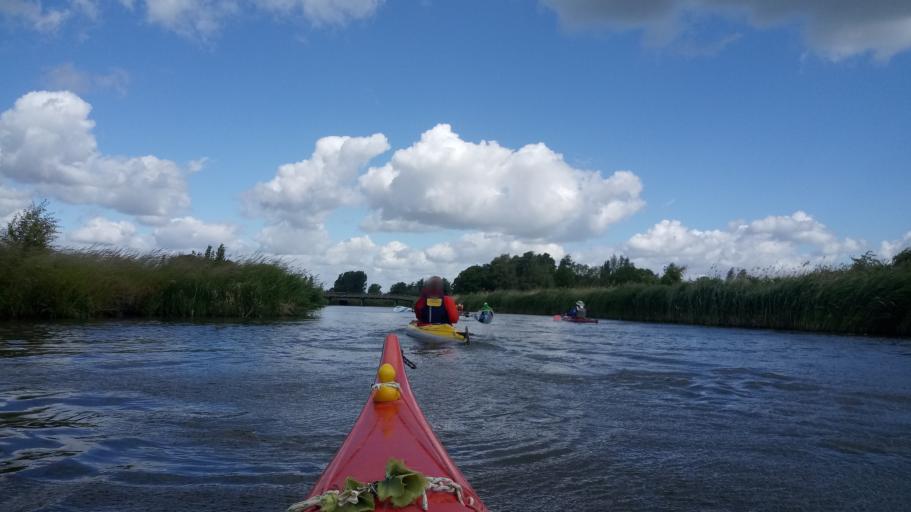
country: NL
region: North Holland
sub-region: Gemeente Enkhuizen
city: Enkhuizen
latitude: 52.7014
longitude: 5.2004
